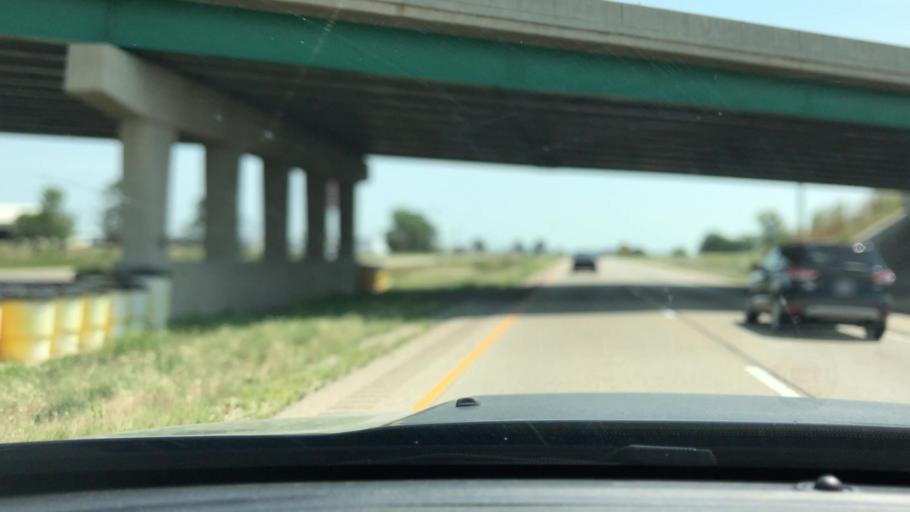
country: US
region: Illinois
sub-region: LaSalle County
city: Peru
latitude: 41.3648
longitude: -89.1525
